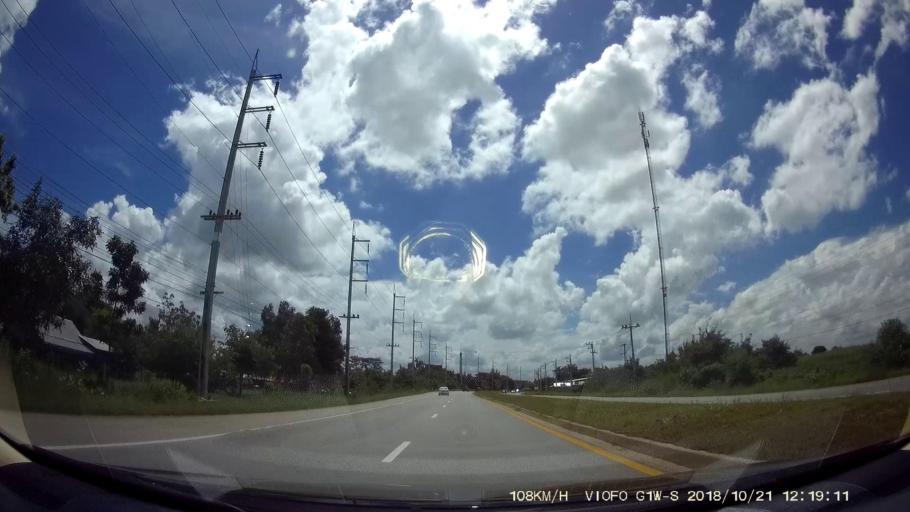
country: TH
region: Nakhon Ratchasima
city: Dan Khun Thot
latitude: 15.3044
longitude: 101.8149
